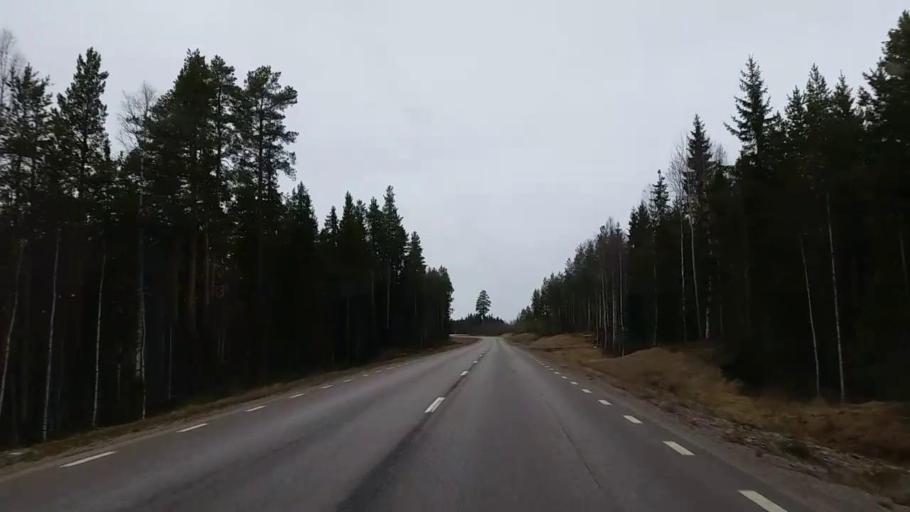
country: SE
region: Gaevleborg
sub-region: Ovanakers Kommun
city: Edsbyn
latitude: 61.1833
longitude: 15.8781
